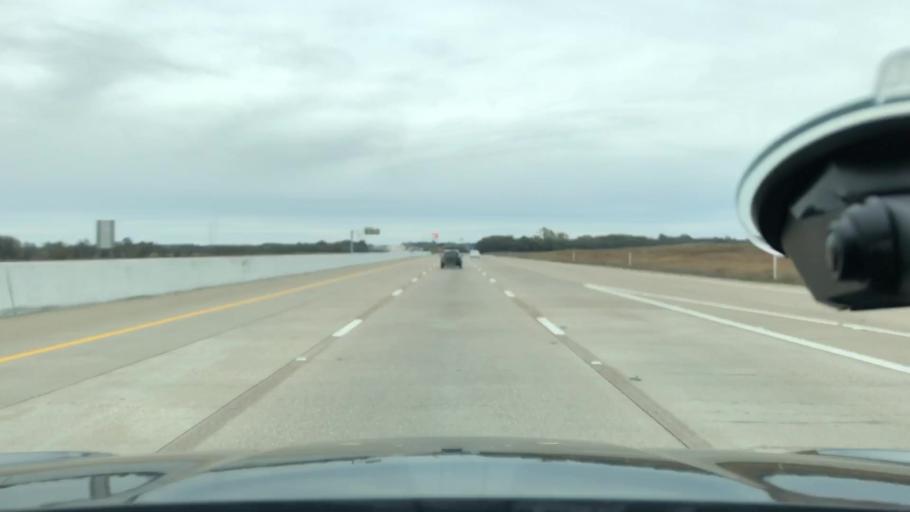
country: US
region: Texas
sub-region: Ellis County
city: Italy
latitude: 32.1798
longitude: -96.9075
